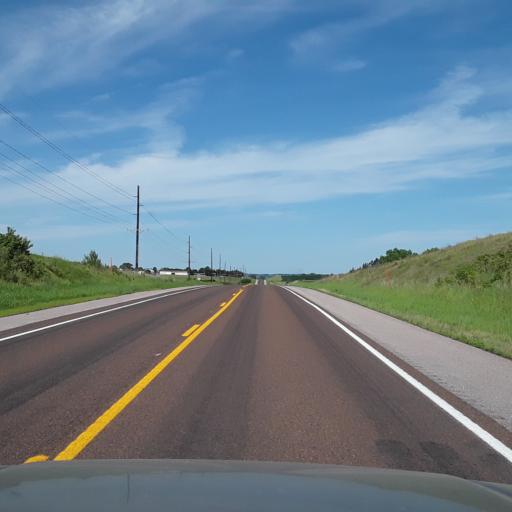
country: US
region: Nebraska
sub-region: Seward County
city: Milford
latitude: 40.8866
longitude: -96.8773
